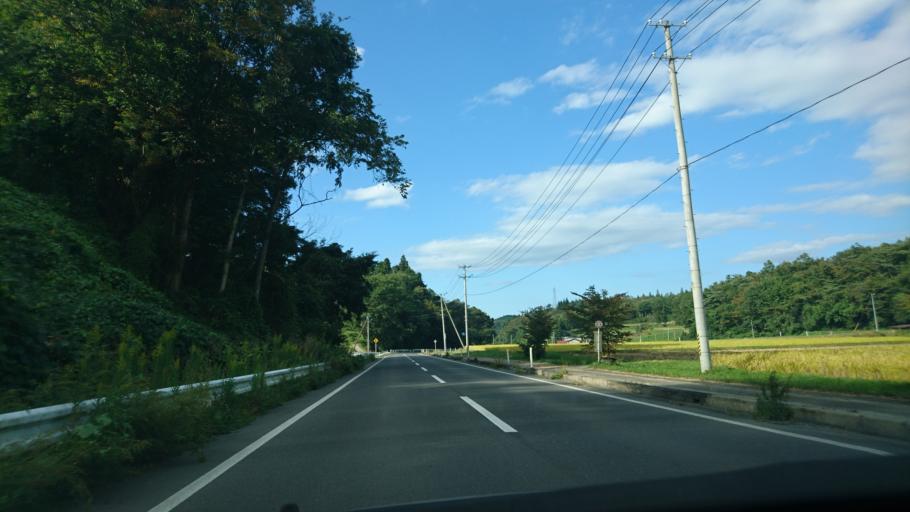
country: JP
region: Iwate
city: Ichinoseki
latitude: 38.8829
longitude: 141.3323
